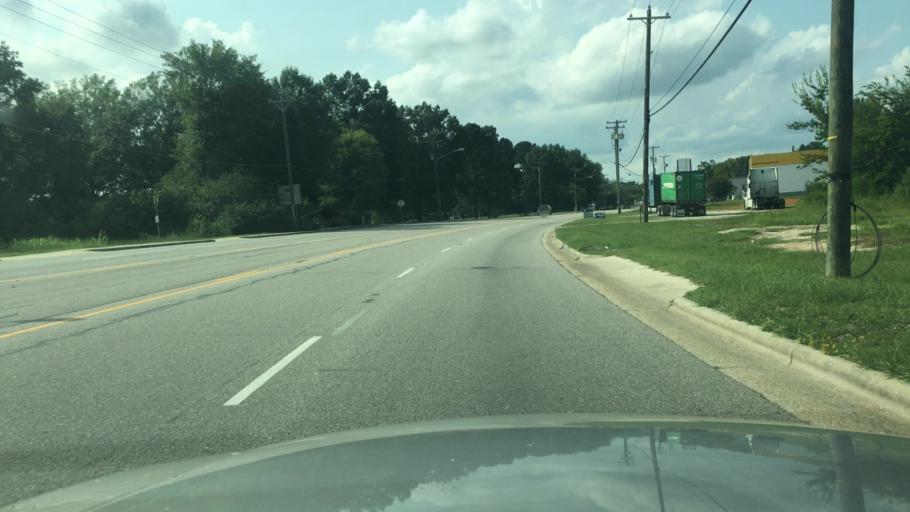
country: US
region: North Carolina
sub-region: Cumberland County
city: Vander
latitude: 35.0133
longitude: -78.8362
